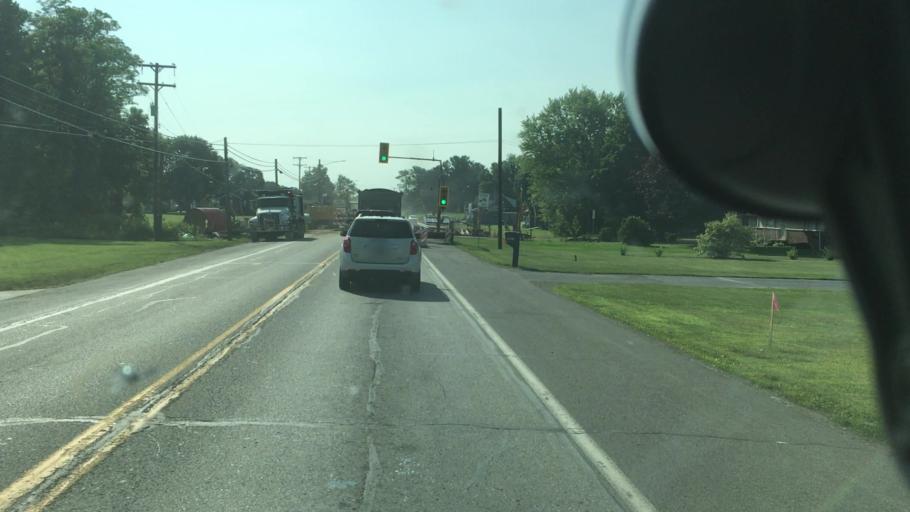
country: US
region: Pennsylvania
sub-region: Lawrence County
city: Bessemer
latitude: 41.0085
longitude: -80.4698
